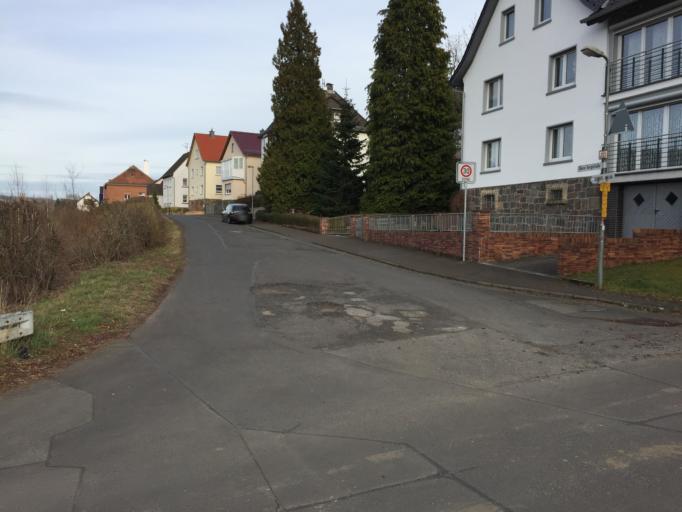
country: DE
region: Hesse
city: Beuern
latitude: 50.6650
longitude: 8.7868
